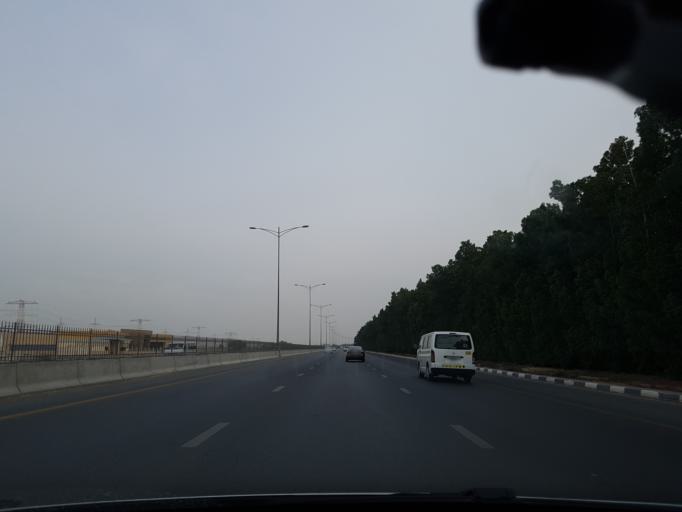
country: AE
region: Ajman
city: Ajman
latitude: 25.3658
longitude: 55.4691
